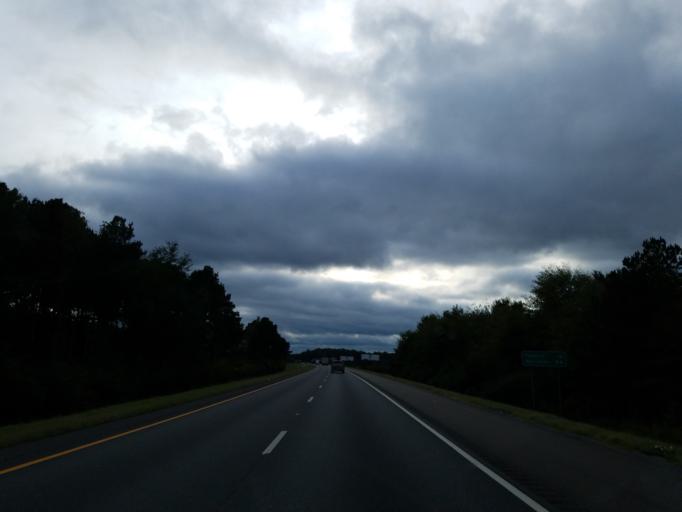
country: US
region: Alabama
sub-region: Tuscaloosa County
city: Tuscaloosa
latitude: 33.1488
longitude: -87.6126
